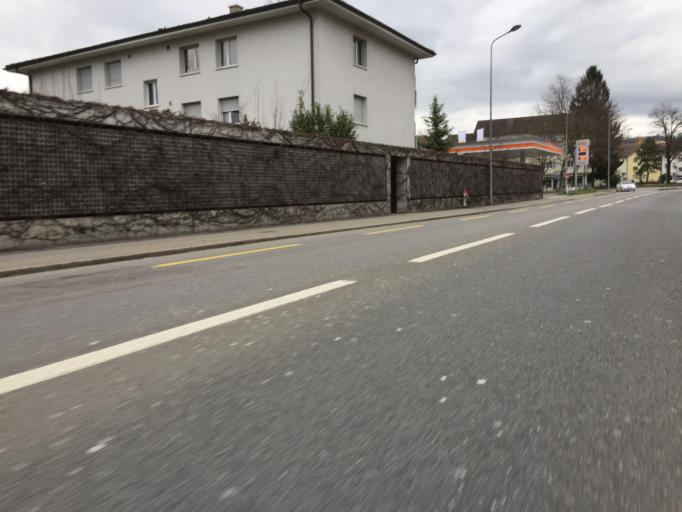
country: CH
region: Bern
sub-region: Emmental District
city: Burgdorf
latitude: 47.0632
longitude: 7.6154
